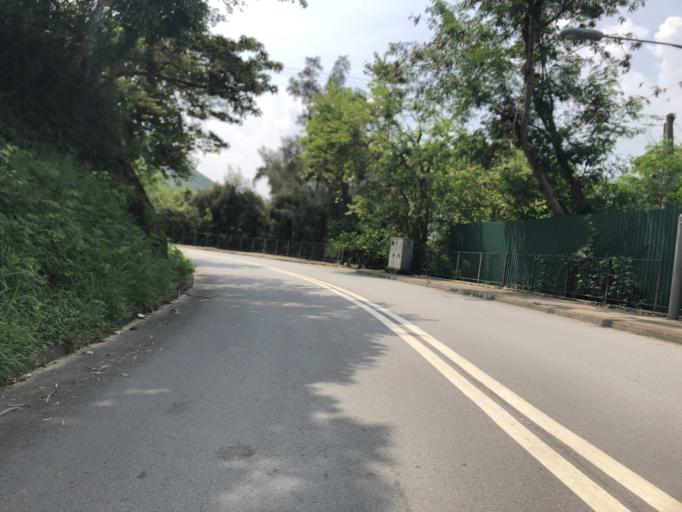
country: CN
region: Guangdong
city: Shatoujiao
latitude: 22.5256
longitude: 114.2156
